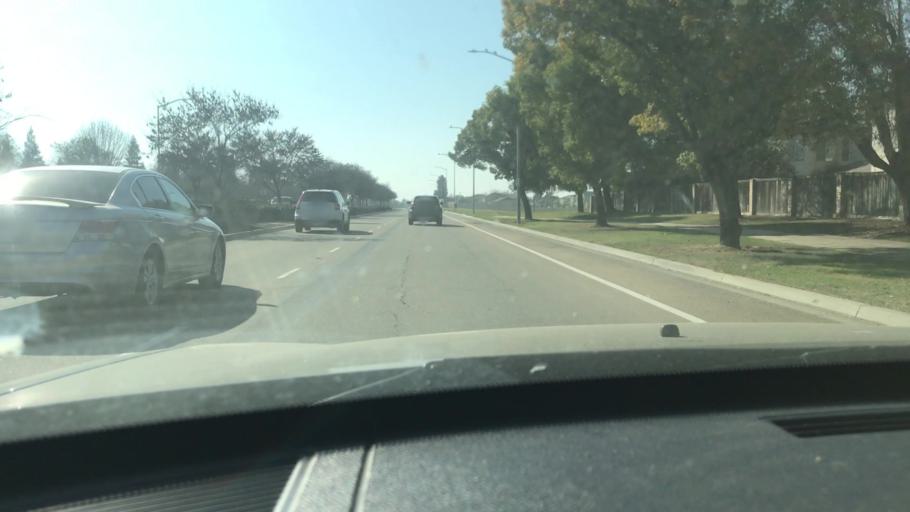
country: US
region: California
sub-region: Fresno County
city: Tarpey Village
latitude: 36.7928
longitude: -119.6641
